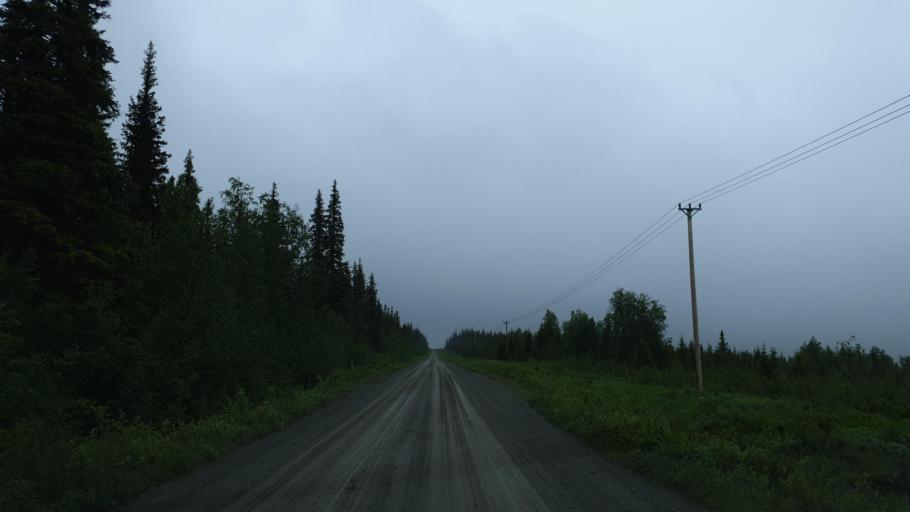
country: SE
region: Vaesterbotten
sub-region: Vilhelmina Kommun
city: Sjoberg
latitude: 65.3217
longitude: 15.9366
